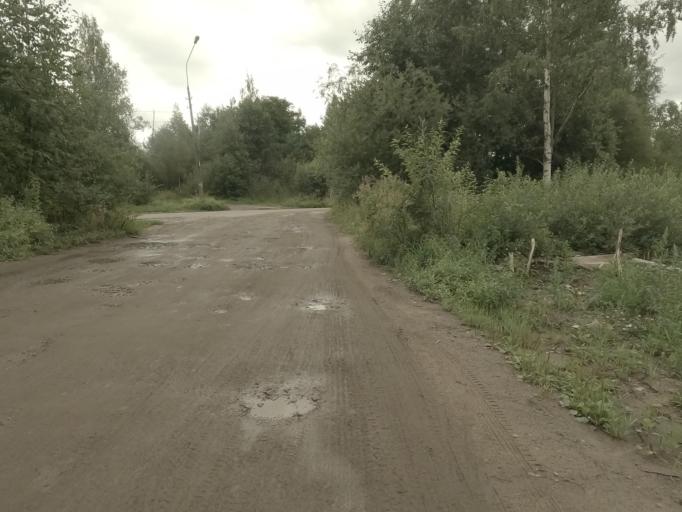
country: RU
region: Leningrad
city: Kirovsk
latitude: 59.8906
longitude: 31.0038
